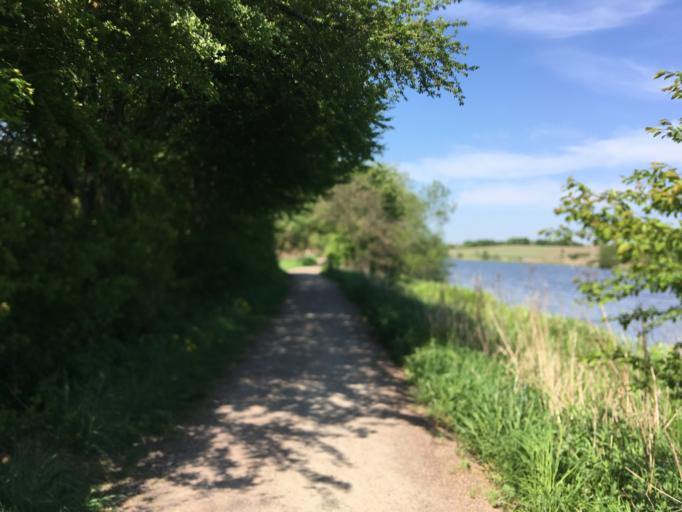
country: SE
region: Skane
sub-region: Staffanstorps Kommun
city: Hjaerup
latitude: 55.6947
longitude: 13.1587
